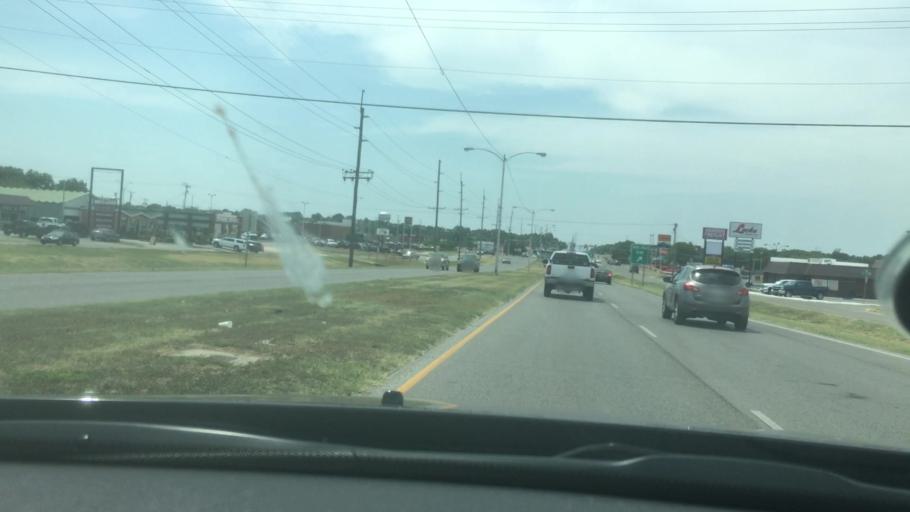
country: US
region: Oklahoma
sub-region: Carter County
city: Ardmore
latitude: 34.1834
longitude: -97.1431
